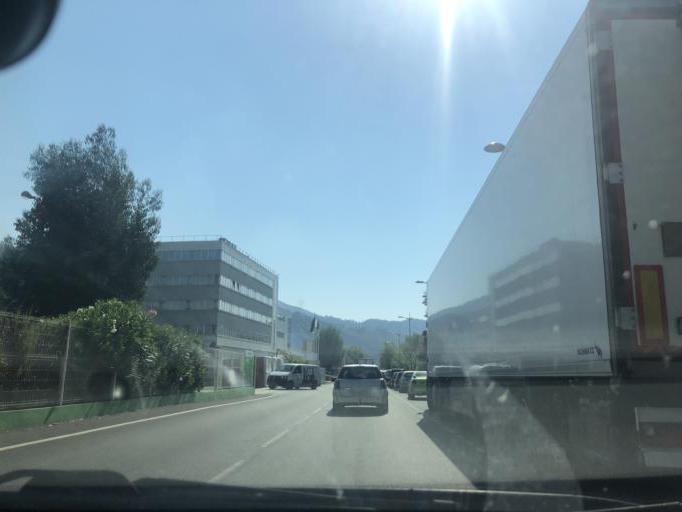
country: FR
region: Provence-Alpes-Cote d'Azur
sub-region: Departement des Alpes-Maritimes
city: Carros
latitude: 43.7884
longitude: 7.2076
